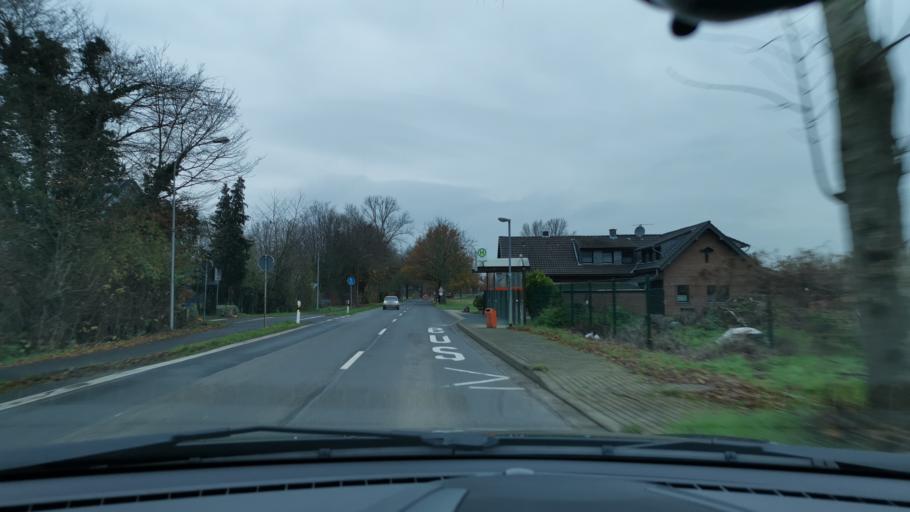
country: DE
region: North Rhine-Westphalia
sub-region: Regierungsbezirk Dusseldorf
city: Neubrueck
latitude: 51.1309
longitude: 6.6455
